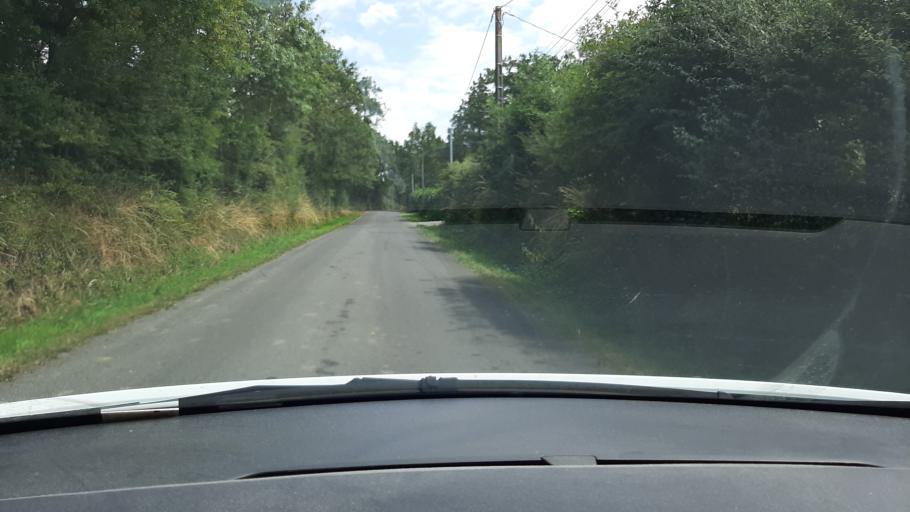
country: FR
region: Pays de la Loire
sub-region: Departement de la Vendee
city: Saint-Etienne-du-Bois
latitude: 46.7845
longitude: -1.5677
